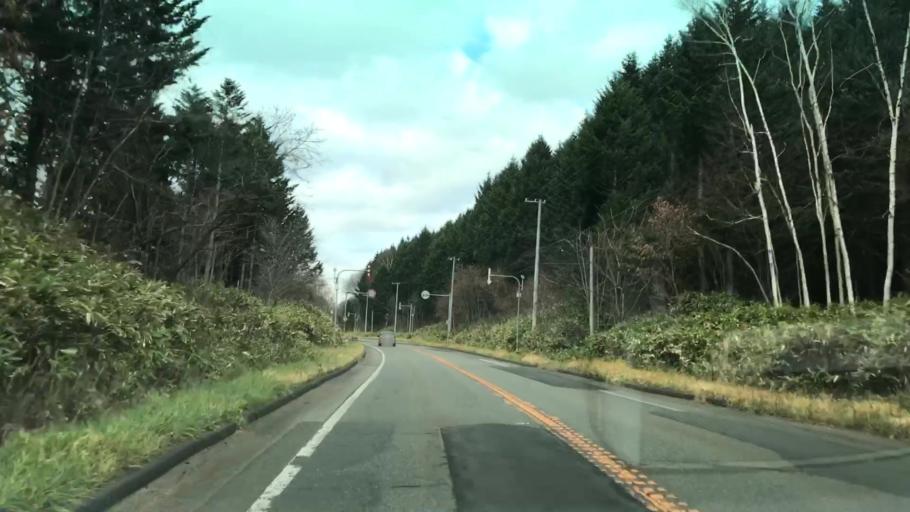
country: JP
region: Hokkaido
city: Shimo-furano
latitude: 42.8949
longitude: 142.4359
